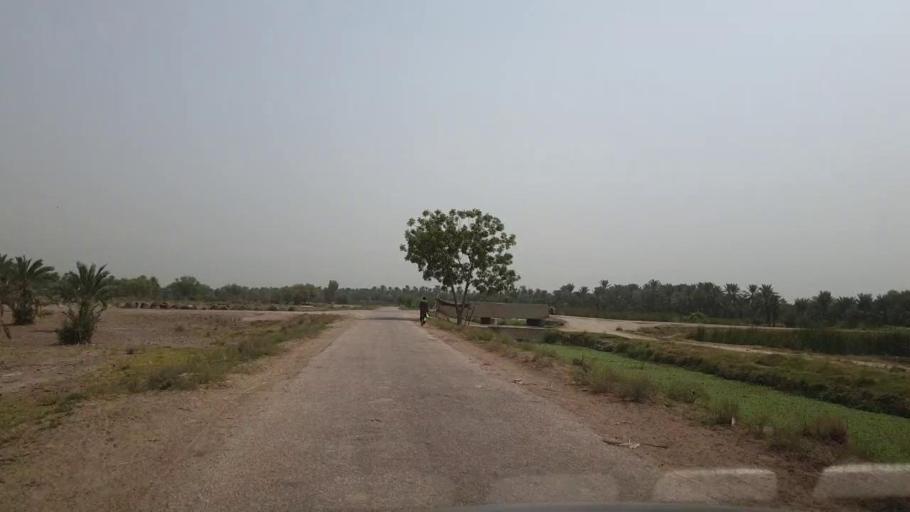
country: PK
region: Sindh
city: Gambat
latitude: 27.4144
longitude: 68.5514
